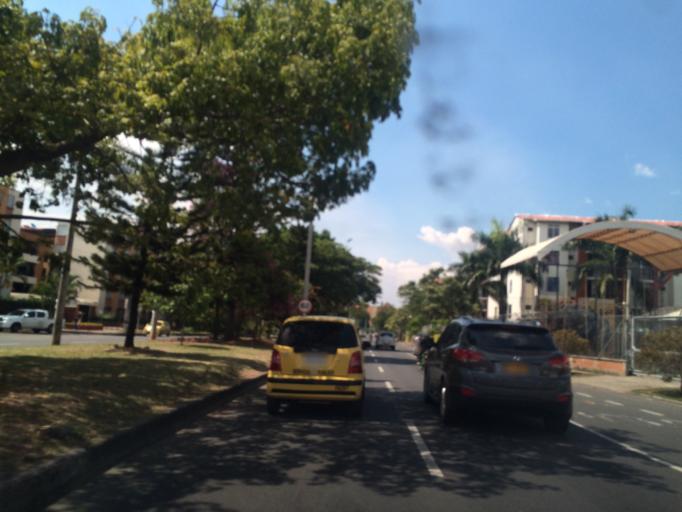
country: CO
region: Valle del Cauca
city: Cali
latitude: 3.4029
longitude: -76.5274
